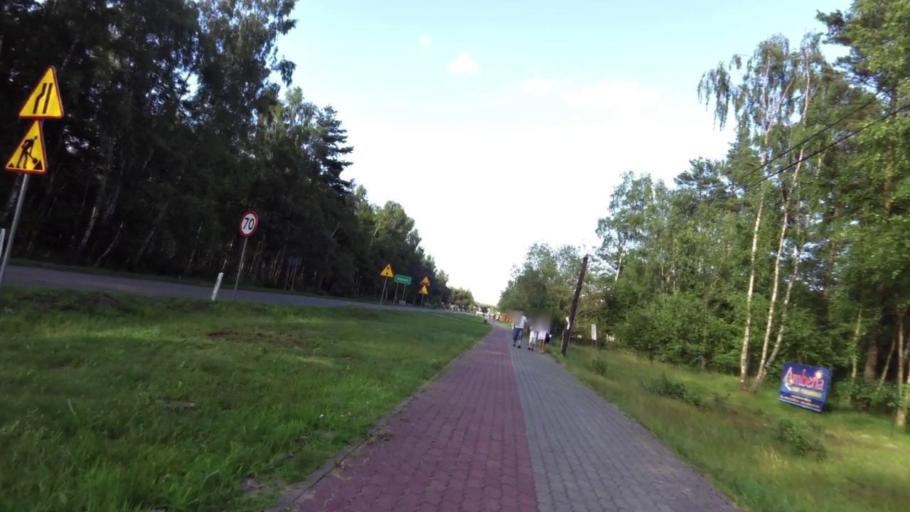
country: PL
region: West Pomeranian Voivodeship
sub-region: Powiat slawienski
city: Darlowo
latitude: 54.3867
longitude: 16.3287
